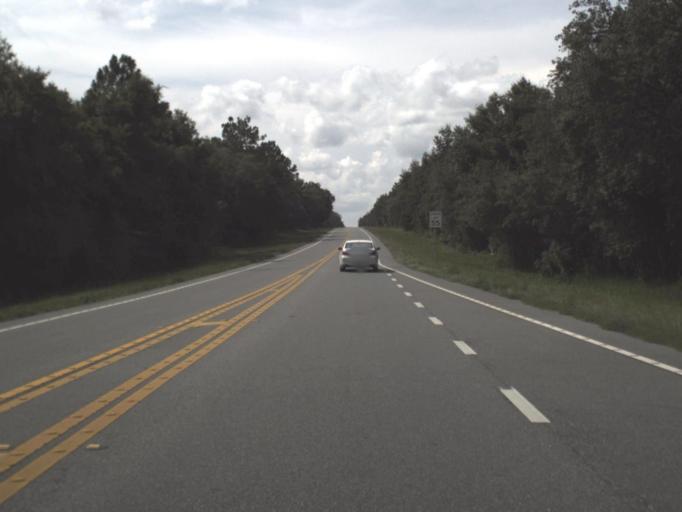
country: US
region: Florida
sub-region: Citrus County
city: Citrus Springs
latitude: 28.9999
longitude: -82.4447
